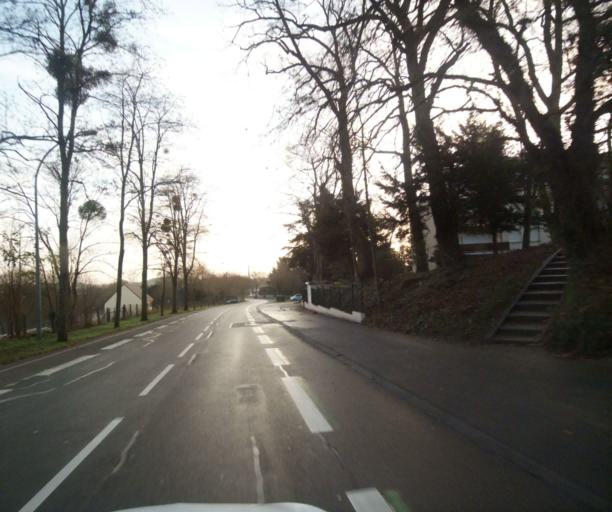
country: FR
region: Pays de la Loire
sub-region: Departement de la Sarthe
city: Sarge-les-le-Mans
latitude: 48.0053
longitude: 0.2312
